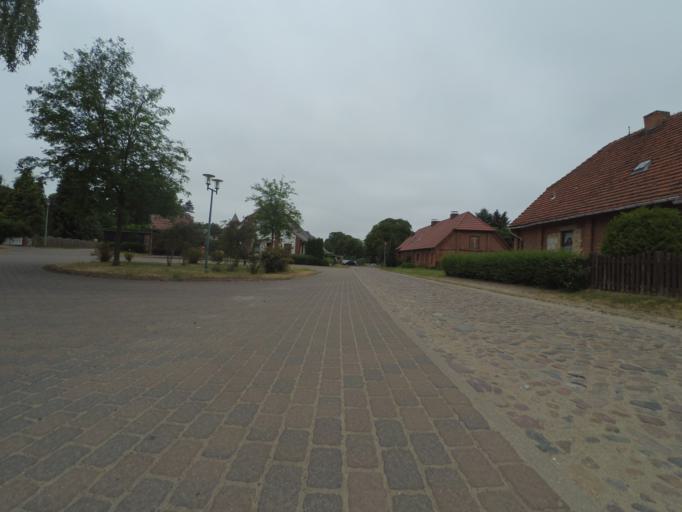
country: DE
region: Mecklenburg-Vorpommern
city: Goldberg
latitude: 53.5636
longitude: 12.1122
